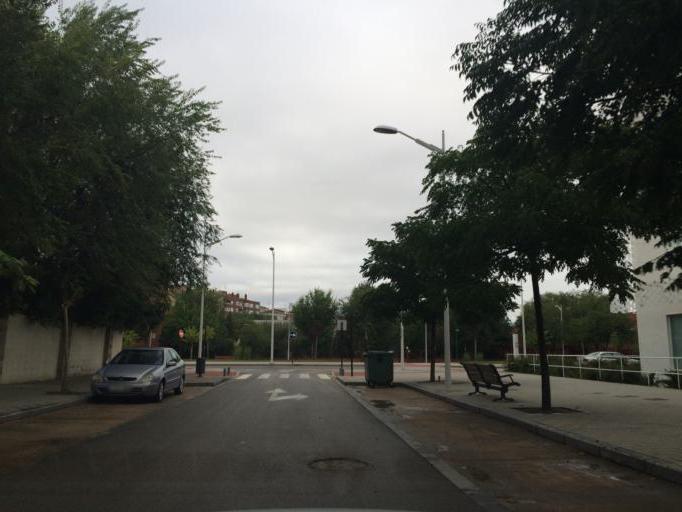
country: ES
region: Castille-La Mancha
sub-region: Provincia de Albacete
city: Albacete
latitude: 39.0060
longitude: -1.8592
